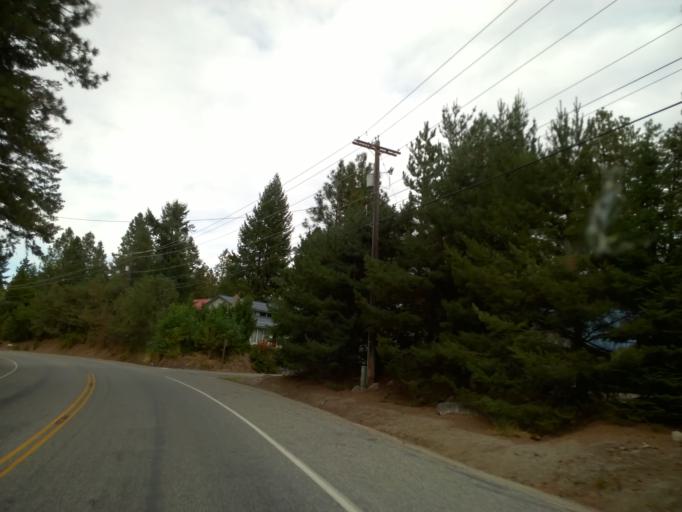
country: US
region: Washington
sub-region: Chelan County
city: Leavenworth
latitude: 47.5781
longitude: -120.6733
